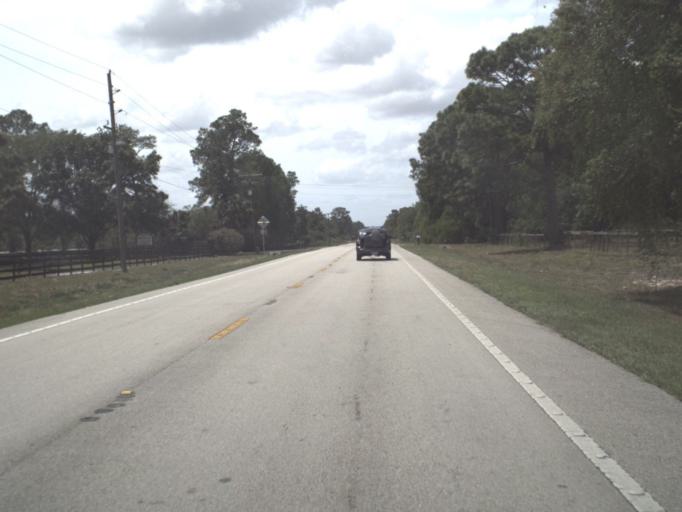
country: US
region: Florida
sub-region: Lake County
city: Mount Plymouth
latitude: 28.8657
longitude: -81.5042
